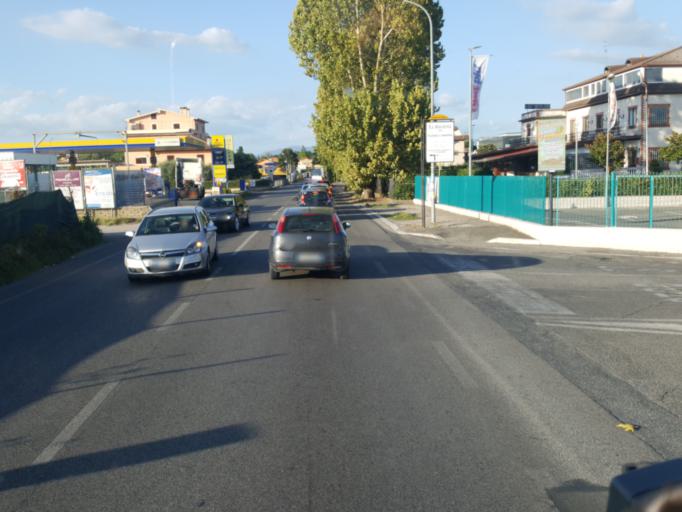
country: IT
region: Latium
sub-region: Citta metropolitana di Roma Capitale
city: Bivio di Capanelle
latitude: 42.1175
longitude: 12.5888
